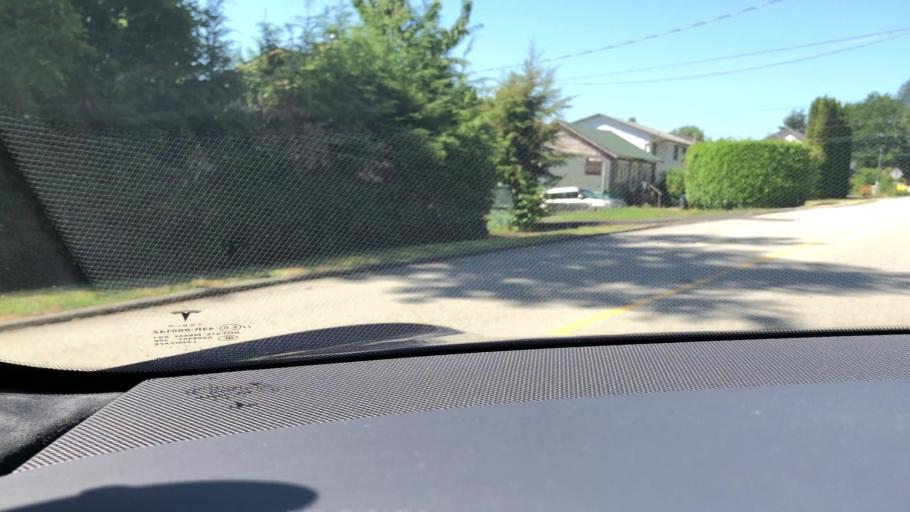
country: CA
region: British Columbia
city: Port Moody
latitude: 49.2454
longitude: -122.8651
